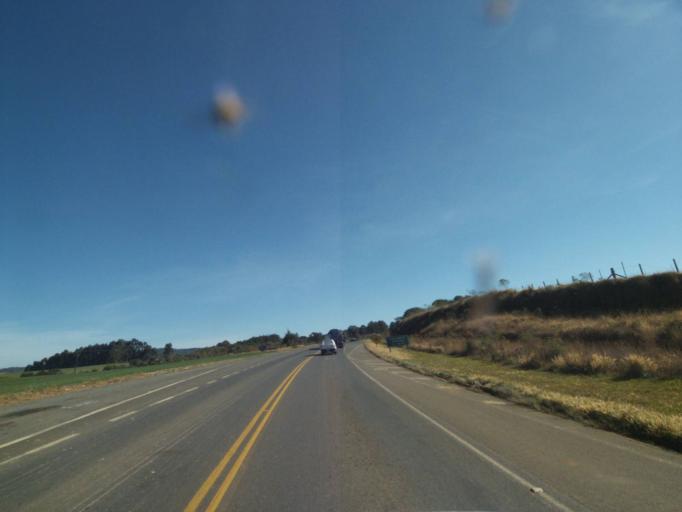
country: BR
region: Parana
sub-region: Tibagi
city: Tibagi
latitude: -24.5259
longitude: -50.4439
